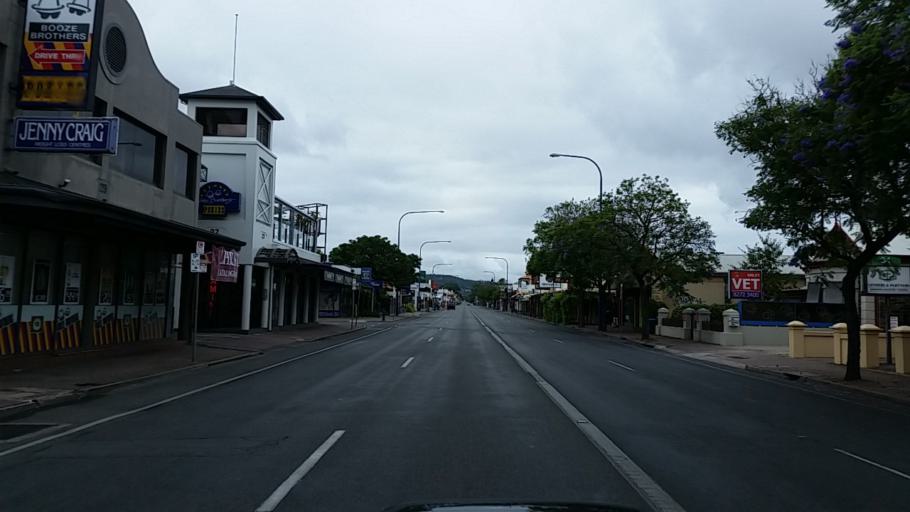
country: AU
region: South Australia
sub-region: Unley
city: Unley
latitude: -34.9427
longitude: 138.6069
